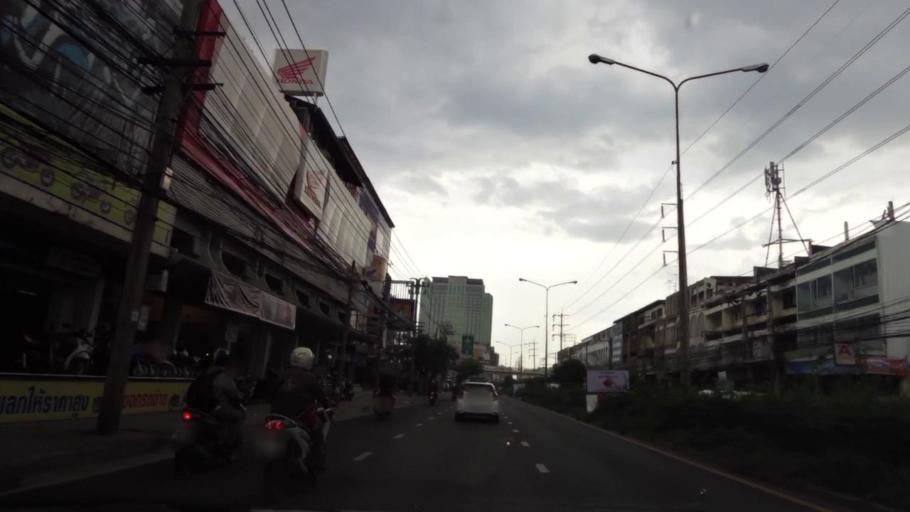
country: TH
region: Bangkok
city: Bang Kapi
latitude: 13.7593
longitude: 100.6456
